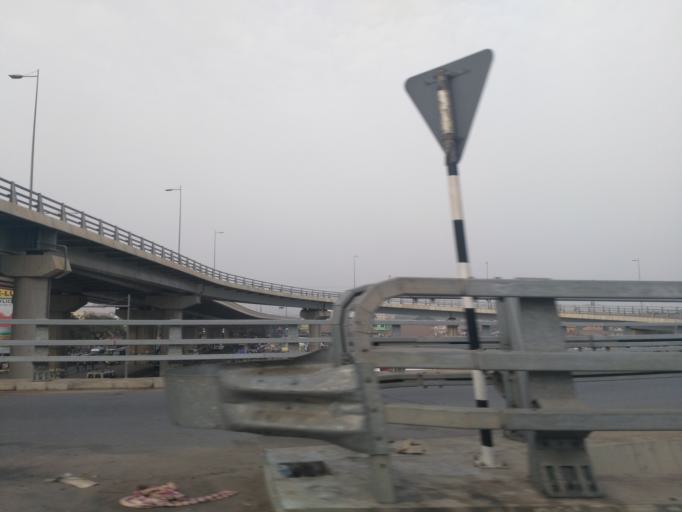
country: GH
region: Greater Accra
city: Accra
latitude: 5.5706
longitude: -0.2158
